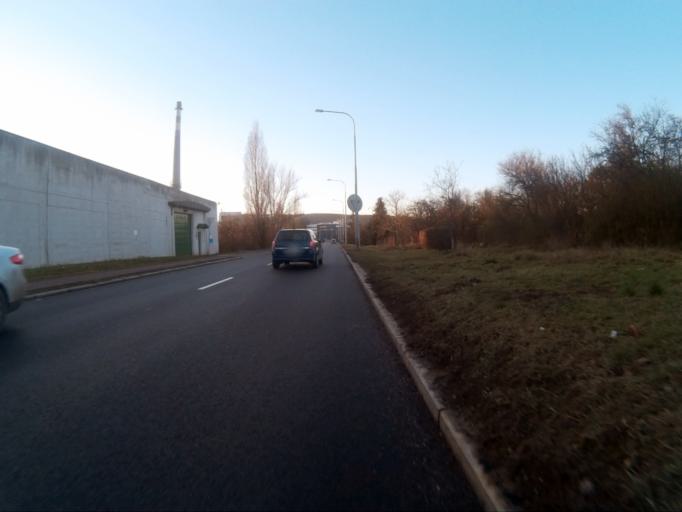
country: CZ
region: South Moravian
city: Moravany
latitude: 49.1762
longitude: 16.5795
